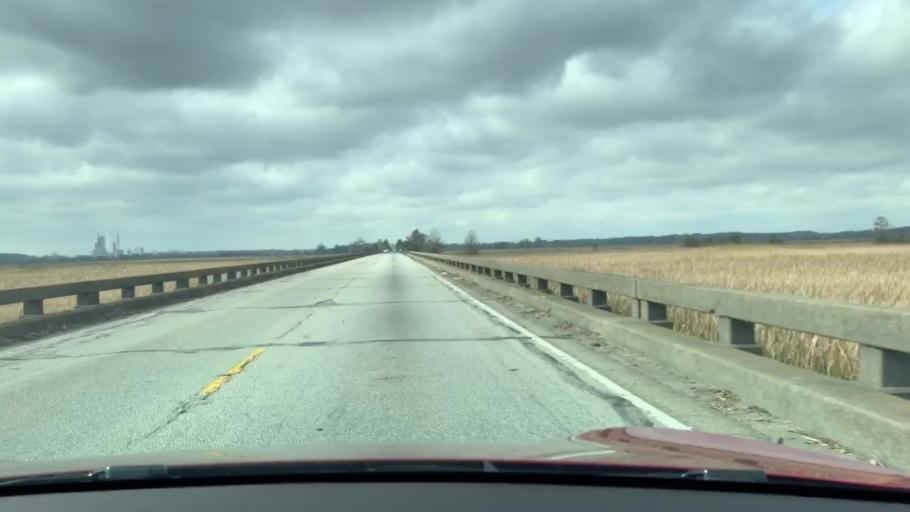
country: US
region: Georgia
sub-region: Chatham County
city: Port Wentworth
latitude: 32.1659
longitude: -81.1263
